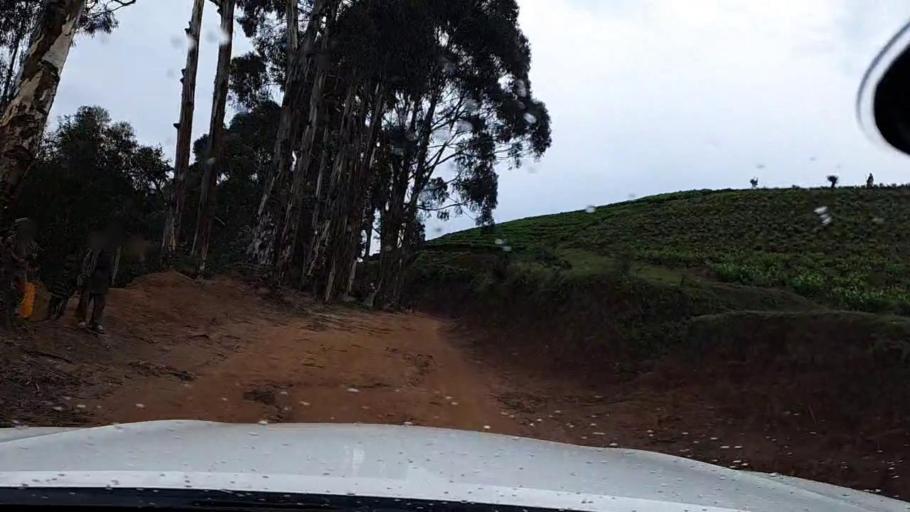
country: RW
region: Southern Province
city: Nzega
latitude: -2.3780
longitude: 29.2443
